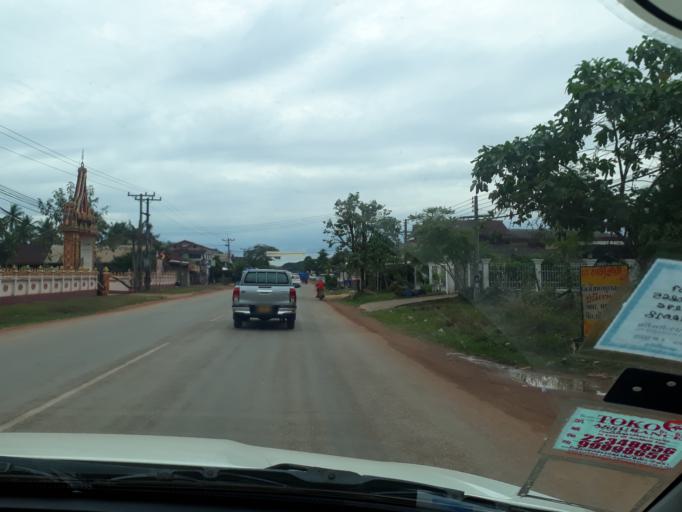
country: LA
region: Vientiane
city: Muang Phon-Hong
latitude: 18.3414
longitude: 102.4320
